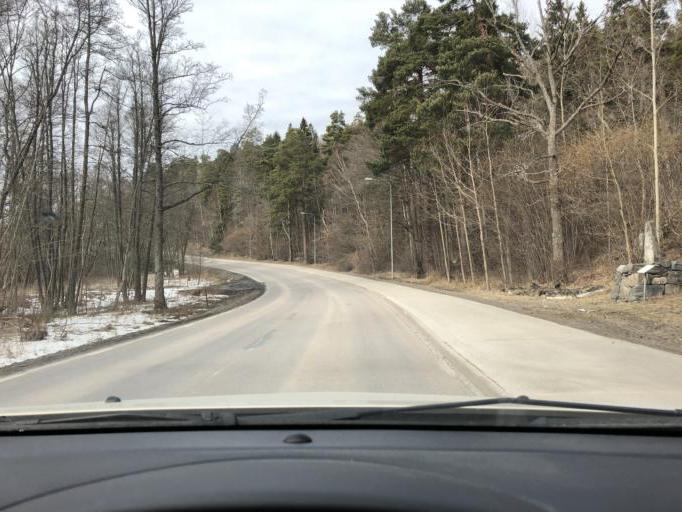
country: SE
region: Stockholm
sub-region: Nacka Kommun
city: Boo
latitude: 59.3330
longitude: 18.3088
